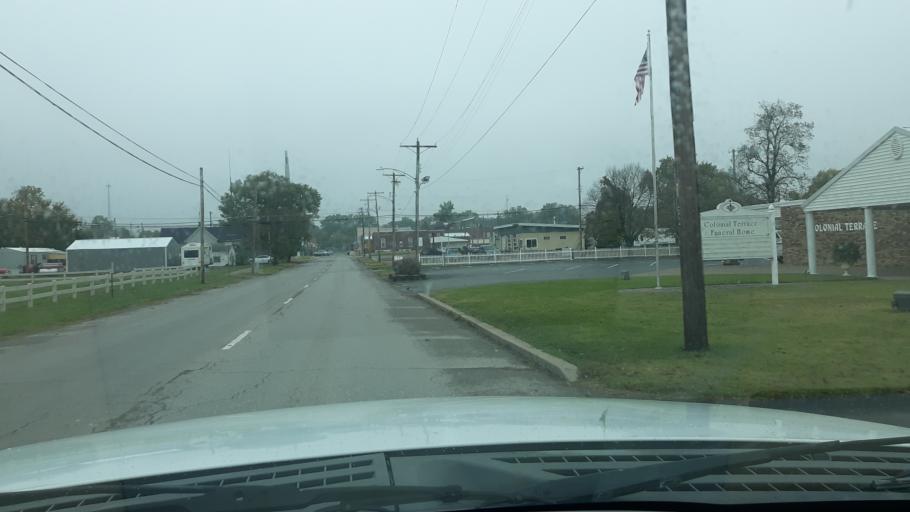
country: US
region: Illinois
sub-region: Saline County
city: Eldorado
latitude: 37.8110
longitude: -88.4362
